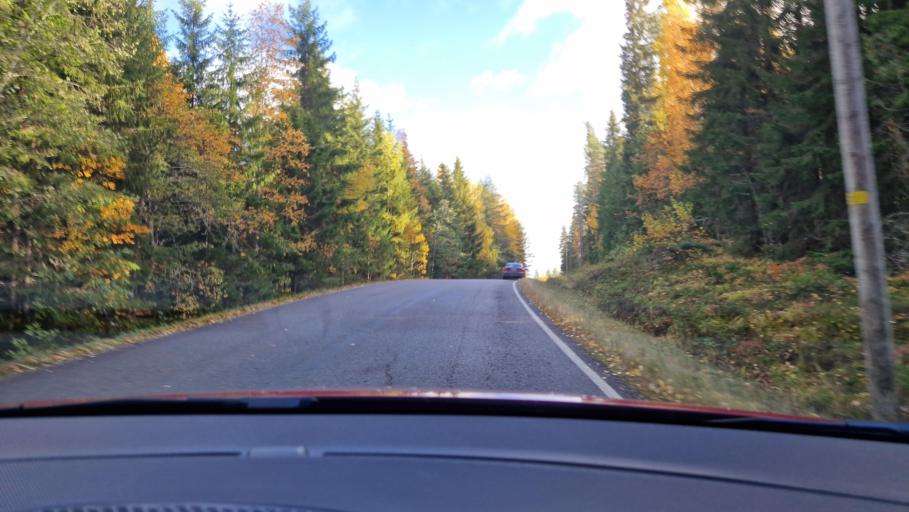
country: FI
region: South Karelia
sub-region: Lappeenranta
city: Lemi
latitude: 60.9901
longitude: 27.7018
